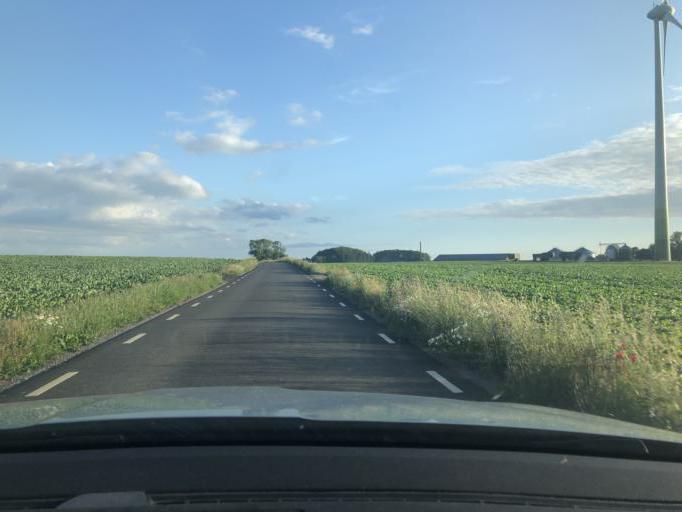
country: SE
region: Skane
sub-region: Simrishamns Kommun
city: Simrishamn
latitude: 55.4715
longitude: 14.1925
